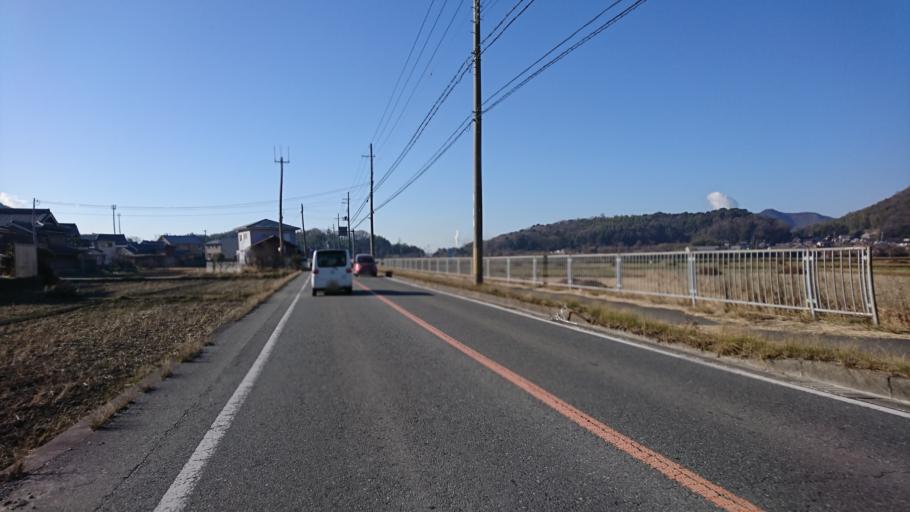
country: JP
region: Hyogo
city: Kakogawacho-honmachi
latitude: 34.8286
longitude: 134.8373
